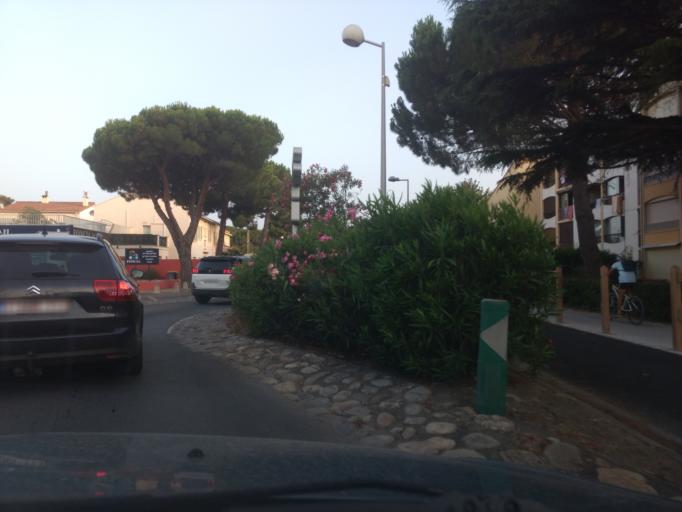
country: FR
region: Languedoc-Roussillon
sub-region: Departement des Pyrenees-Orientales
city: Argelers
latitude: 42.5596
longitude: 3.0412
